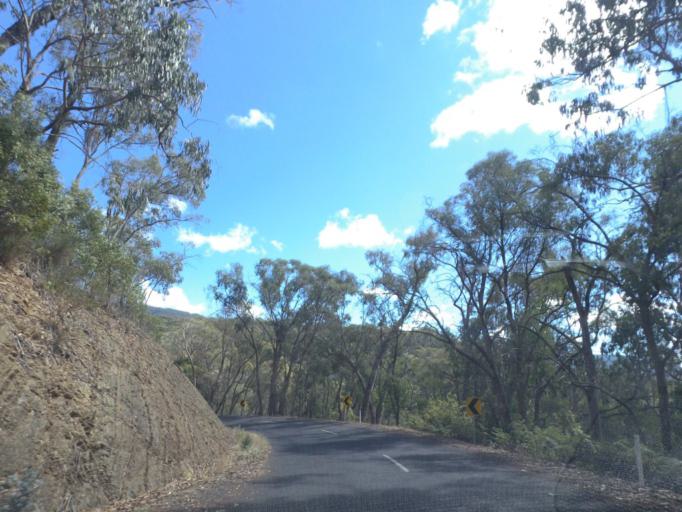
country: AU
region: Victoria
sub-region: Murrindindi
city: Alexandra
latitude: -37.3372
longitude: 145.9582
